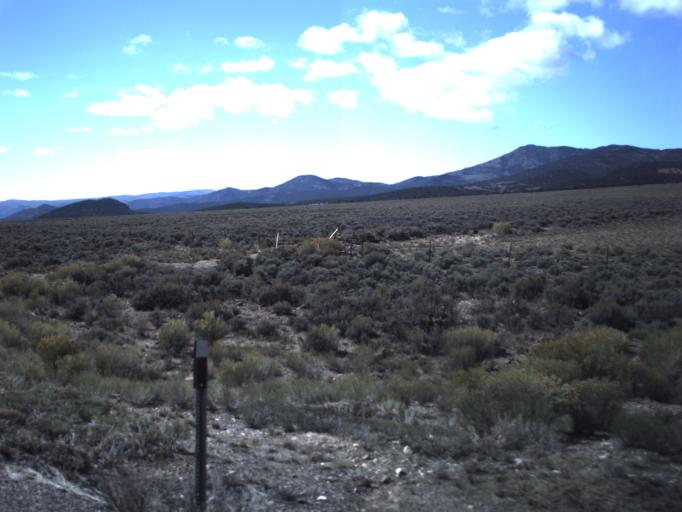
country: US
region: Utah
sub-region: Wayne County
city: Loa
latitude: 38.3831
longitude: -111.9351
